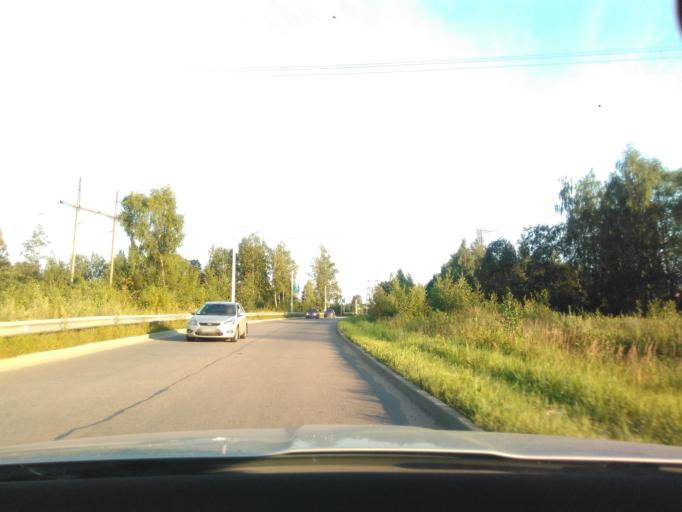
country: RU
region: Tverskaya
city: Konakovo
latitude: 56.7456
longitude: 36.7769
